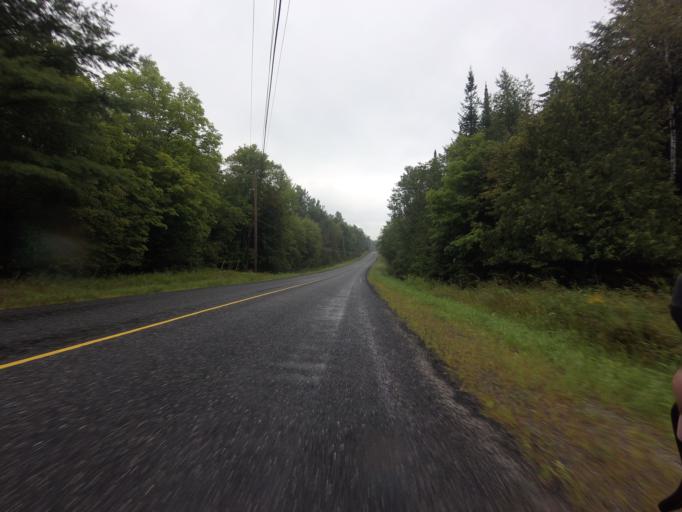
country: CA
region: Ontario
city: Perth
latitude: 45.0647
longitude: -76.5108
